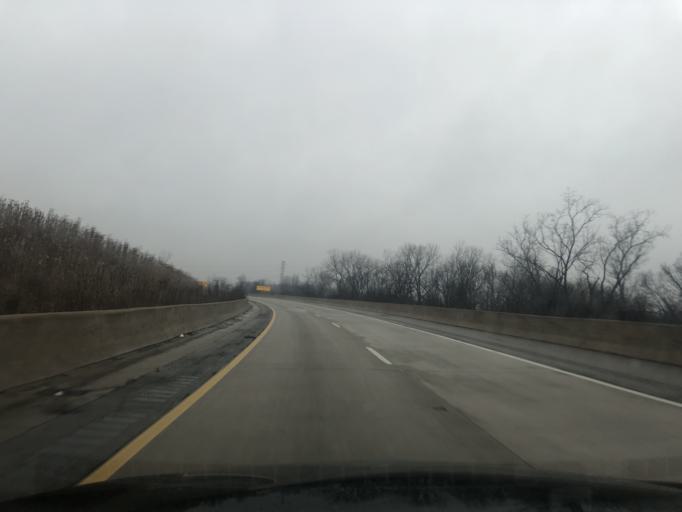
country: US
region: Michigan
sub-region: Wayne County
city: Woodhaven
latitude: 42.1904
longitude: -83.2485
